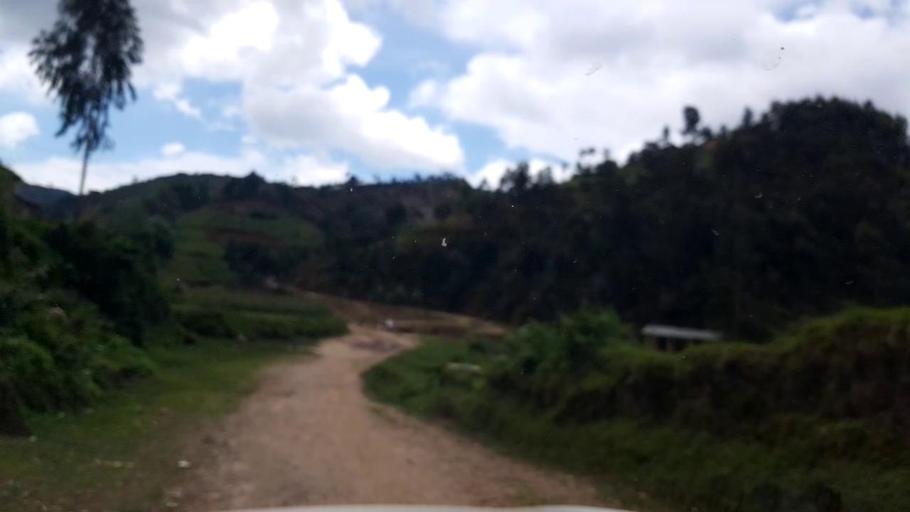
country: RW
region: Western Province
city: Kibuye
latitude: -1.9053
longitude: 29.4560
